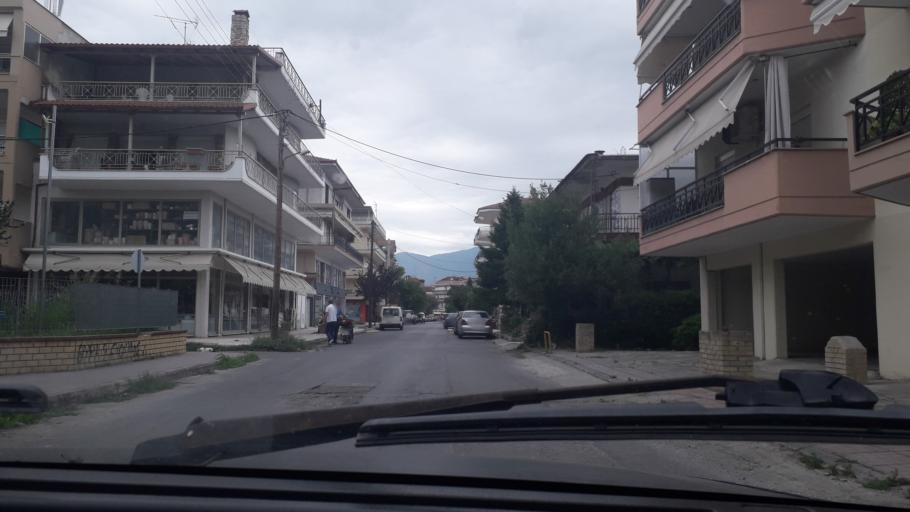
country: GR
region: Central Macedonia
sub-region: Nomos Pellis
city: Aridaia
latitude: 40.9710
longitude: 22.0631
